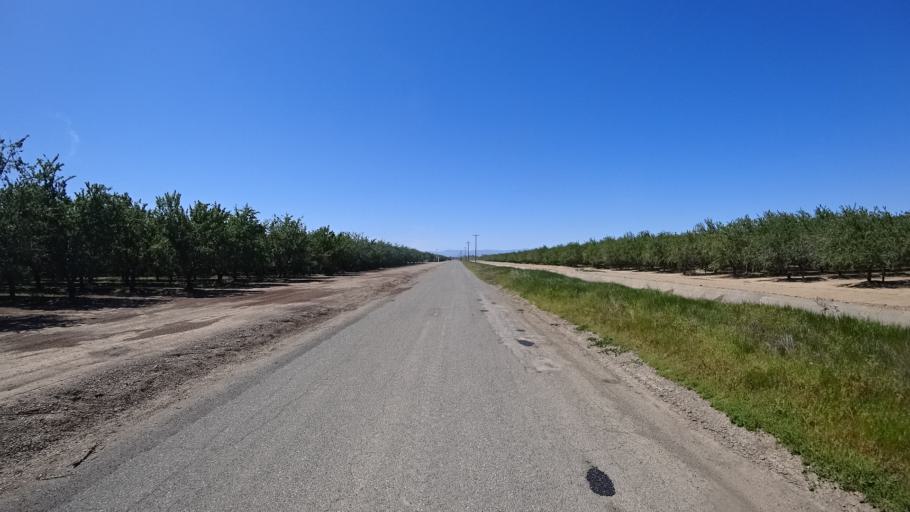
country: US
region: California
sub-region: Glenn County
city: Orland
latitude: 39.7322
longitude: -122.1175
